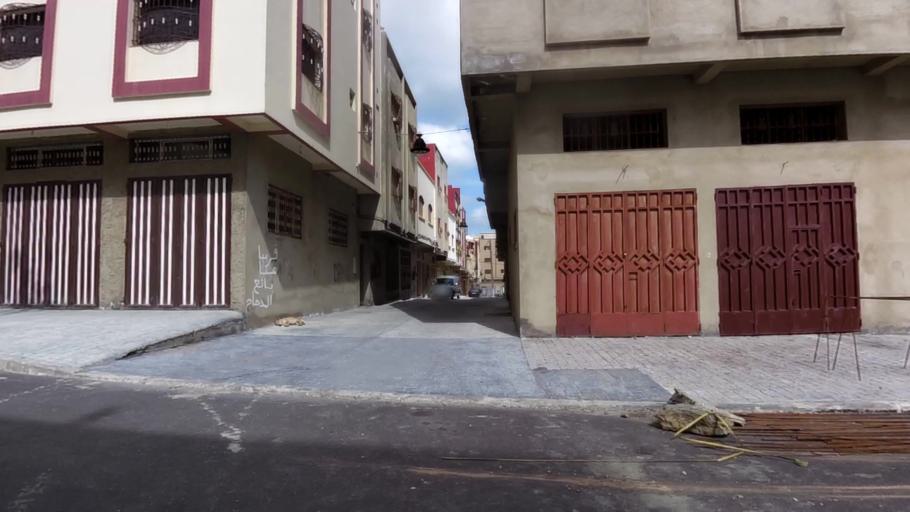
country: MA
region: Tanger-Tetouan
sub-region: Tanger-Assilah
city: Tangier
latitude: 35.7652
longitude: -5.7603
